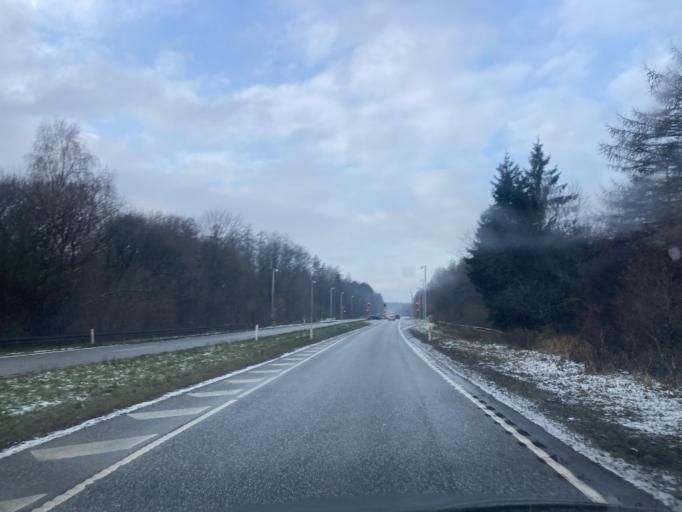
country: DK
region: Zealand
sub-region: Holbaek Kommune
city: Jyderup
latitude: 55.6642
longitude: 11.3942
